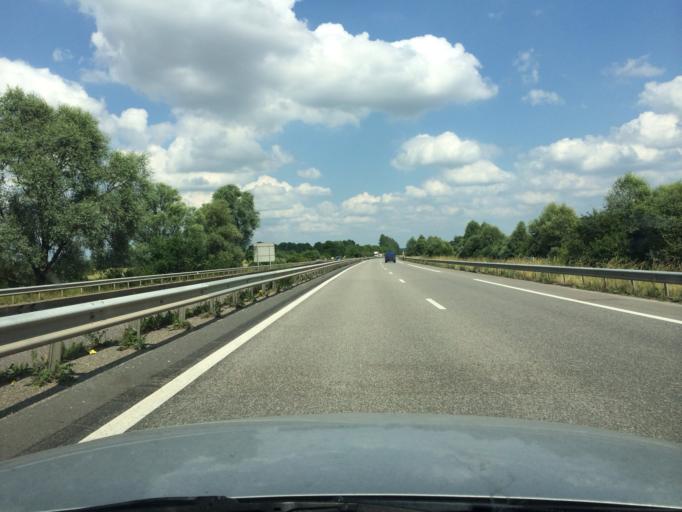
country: FR
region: Lorraine
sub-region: Departement de la Moselle
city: Reding
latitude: 48.7377
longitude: 7.0950
